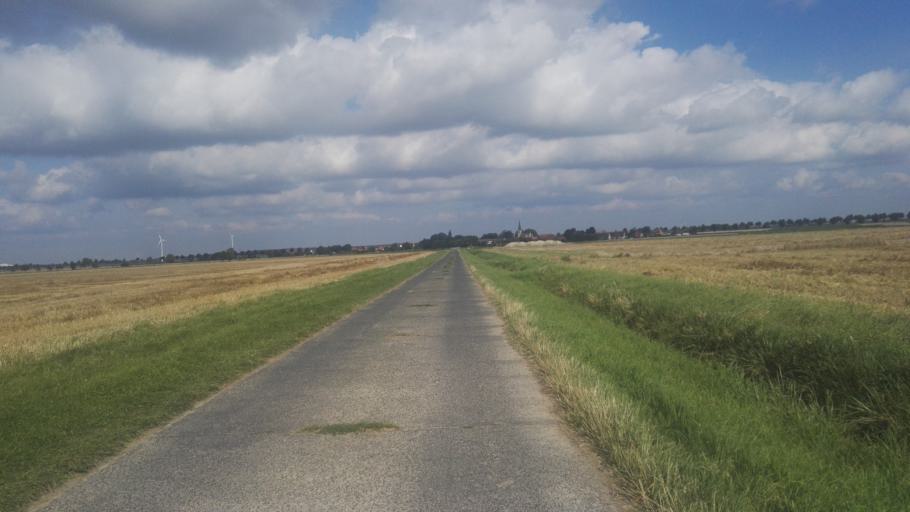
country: DE
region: Lower Saxony
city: Schellerten
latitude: 52.1602
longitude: 10.0495
